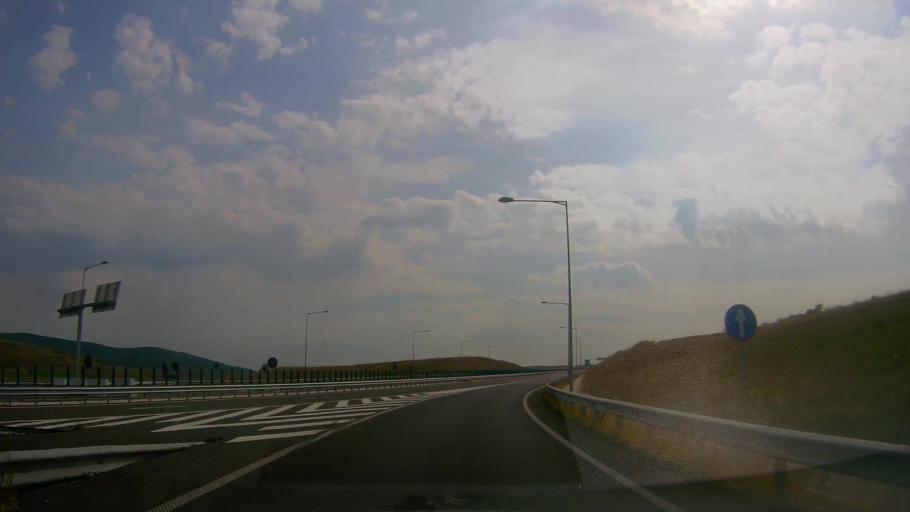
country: RO
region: Cluj
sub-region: Comuna Baciu
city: Mera
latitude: 46.8080
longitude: 23.4206
